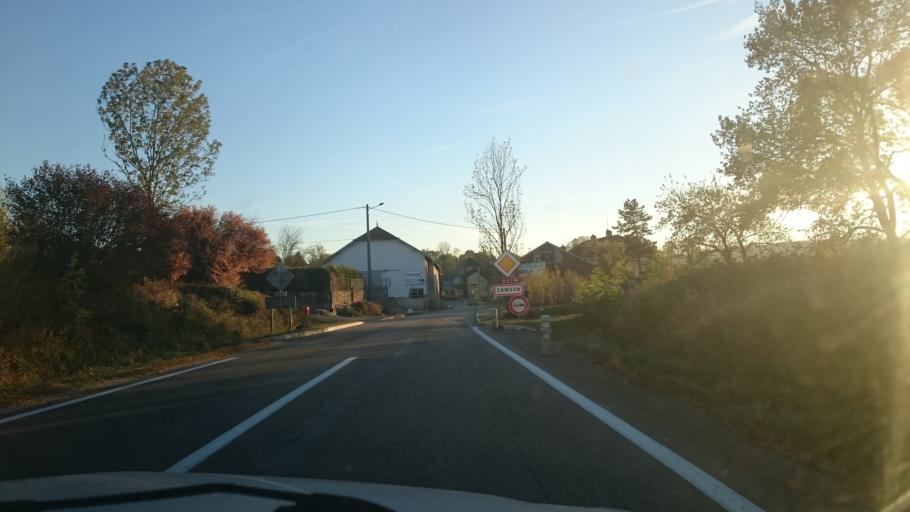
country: FR
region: Franche-Comte
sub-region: Departement du Doubs
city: Quingey
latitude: 47.0549
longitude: 5.8802
